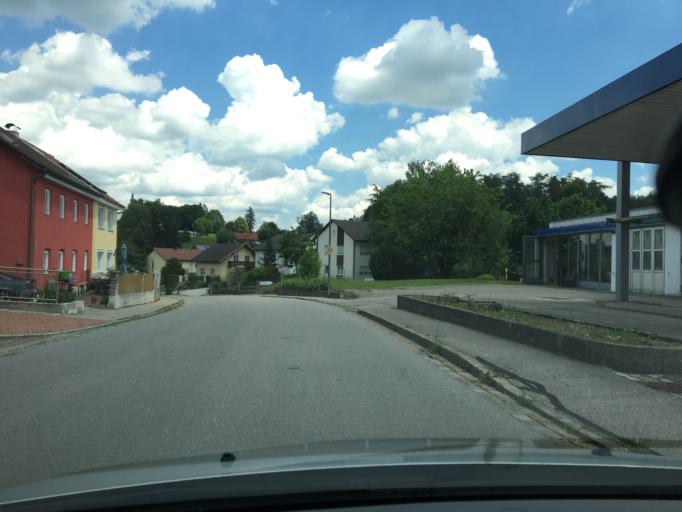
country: DE
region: Bavaria
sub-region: Upper Bavaria
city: Neumarkt-Sankt Veit
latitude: 48.3544
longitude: 12.5119
